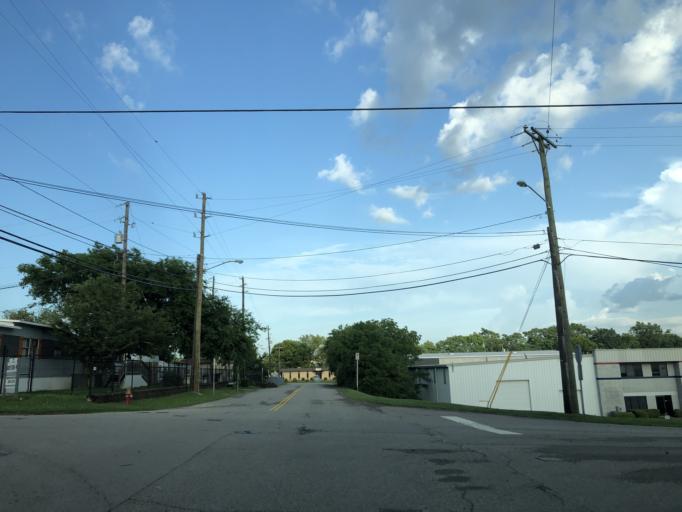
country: US
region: Tennessee
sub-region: Davidson County
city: Nashville
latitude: 36.1373
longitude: -86.7324
